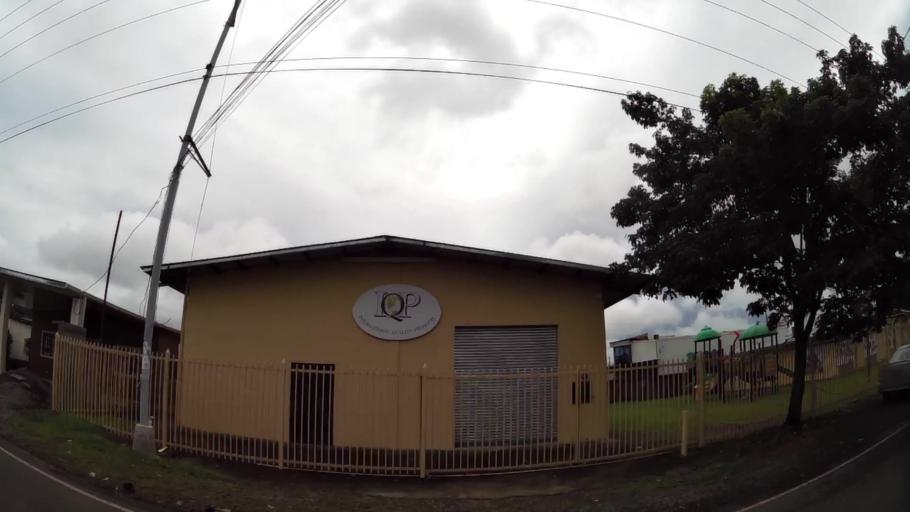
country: PA
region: Chiriqui
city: David
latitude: 8.4362
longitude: -82.4274
